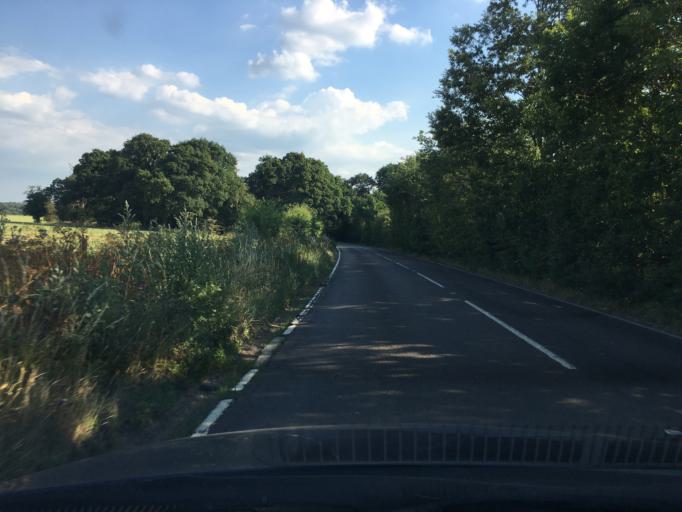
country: GB
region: England
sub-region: Bracknell Forest
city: Binfield
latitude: 51.4021
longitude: -0.7985
